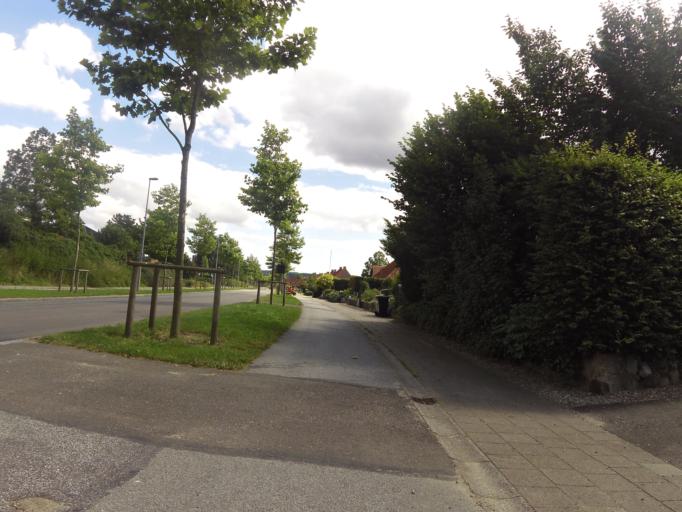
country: DK
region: South Denmark
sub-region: Haderslev Kommune
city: Haderslev
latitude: 55.2527
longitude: 9.4574
